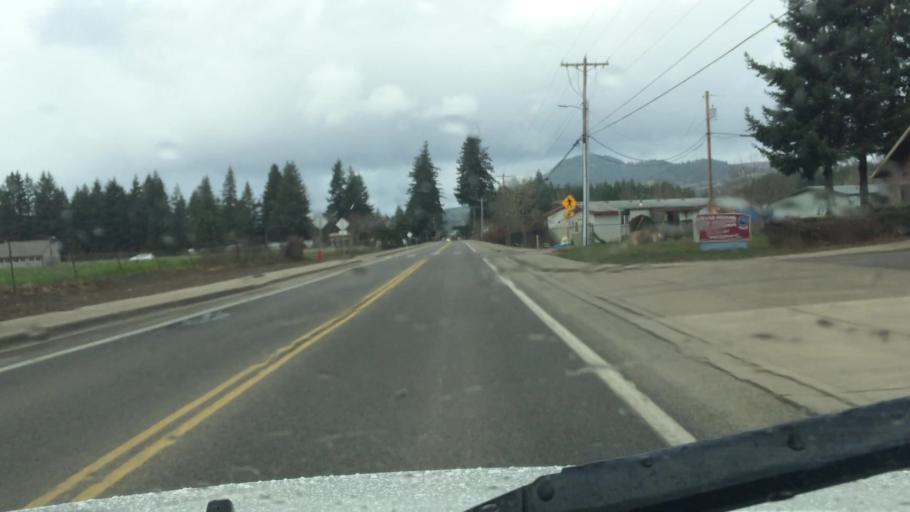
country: US
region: Oregon
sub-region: Polk County
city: Grand Ronde
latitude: 45.0665
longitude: -123.6119
